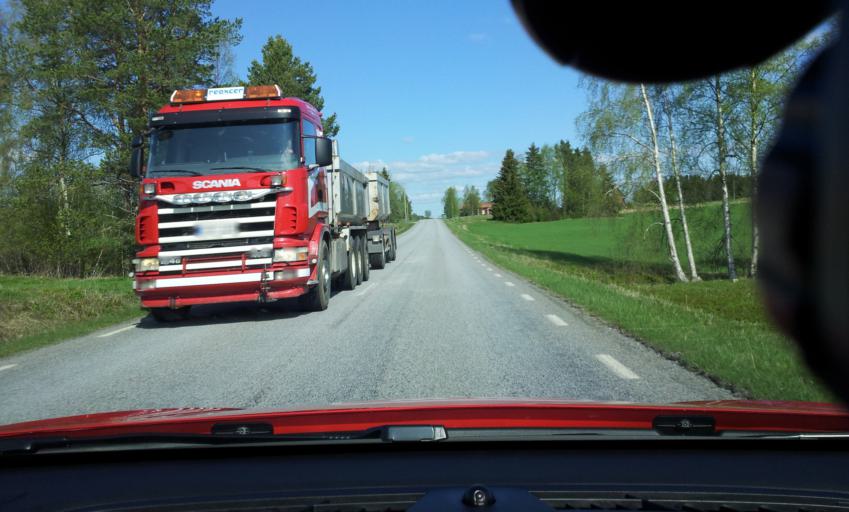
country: SE
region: Jaemtland
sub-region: Krokoms Kommun
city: Krokom
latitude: 63.1409
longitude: 14.1855
